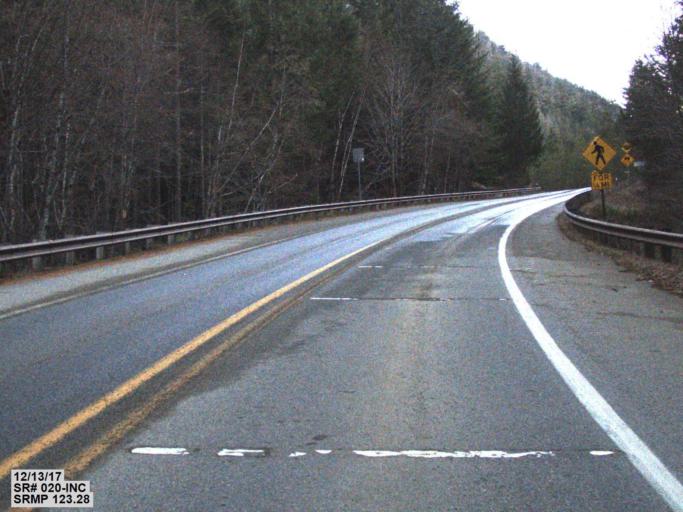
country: US
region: Washington
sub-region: Snohomish County
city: Darrington
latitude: 48.6998
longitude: -121.2129
